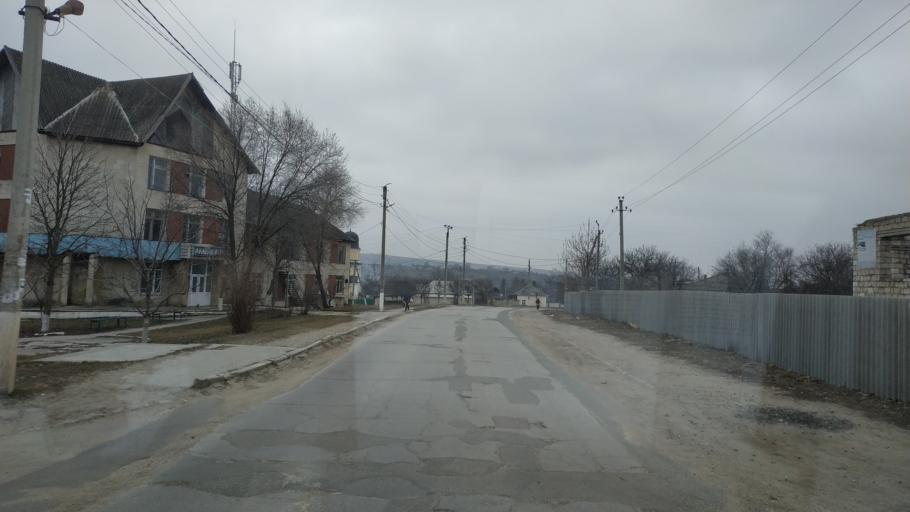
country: MD
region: Hincesti
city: Hincesti
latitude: 46.8858
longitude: 28.4120
